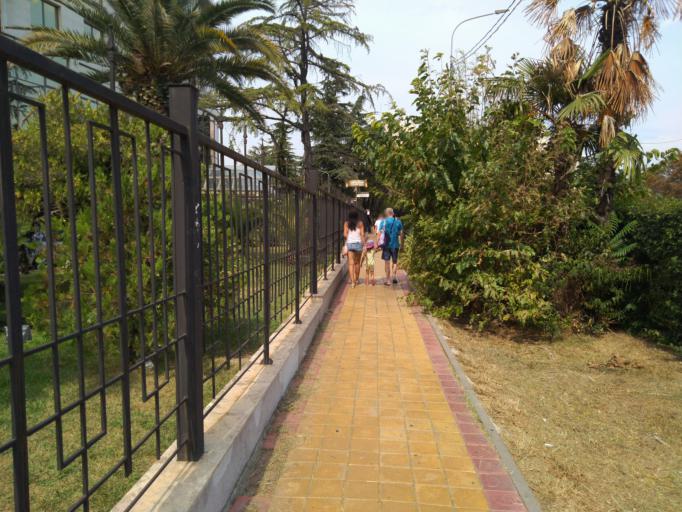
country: RU
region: Krasnodarskiy
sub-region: Sochi City
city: Sochi
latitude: 43.5946
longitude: 39.7203
